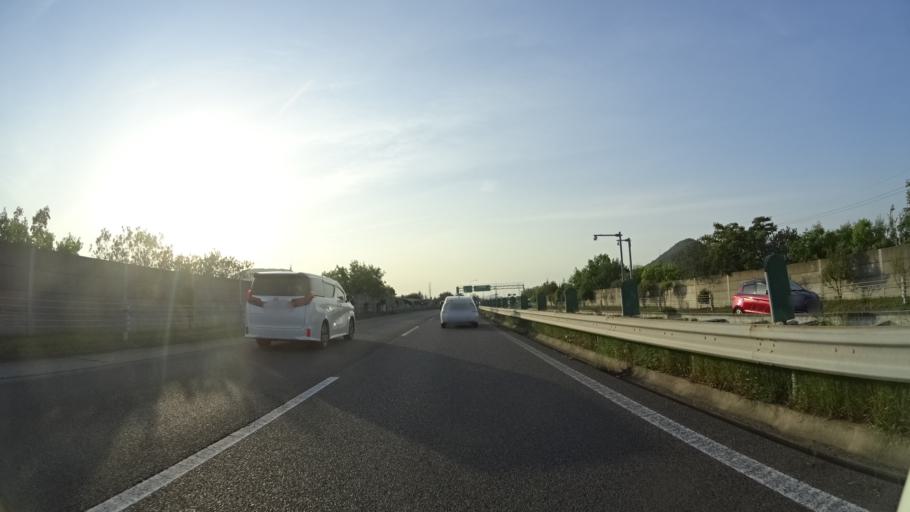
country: JP
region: Kagawa
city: Sakaidecho
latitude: 34.2922
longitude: 133.8478
